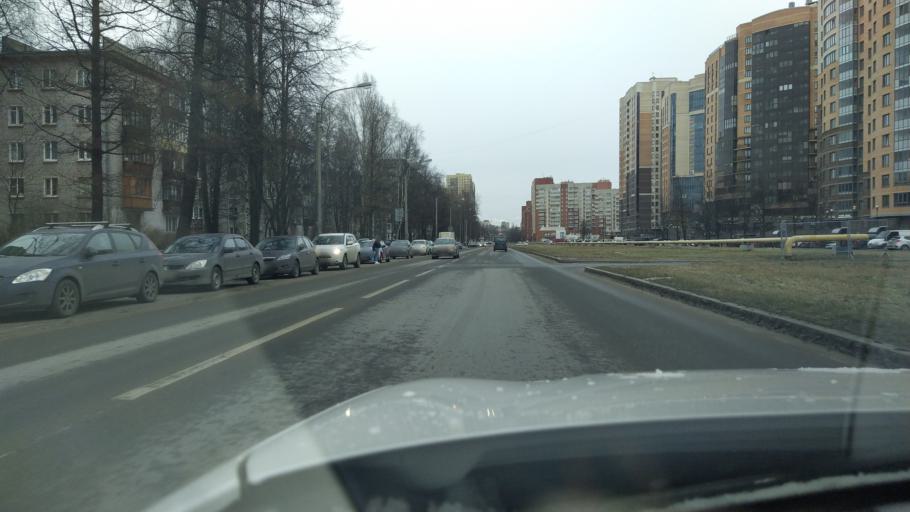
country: RU
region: Leningrad
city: Akademicheskoe
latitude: 60.0039
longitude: 30.3988
